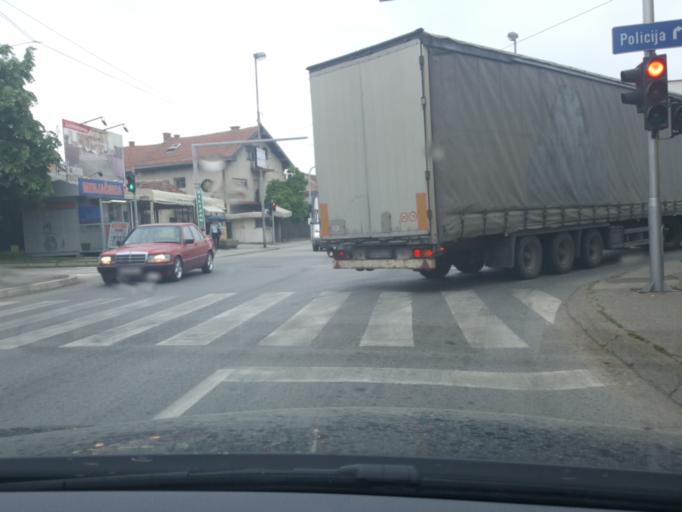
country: RS
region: Central Serbia
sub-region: Kolubarski Okrug
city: Valjevo
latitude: 44.2737
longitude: 19.8800
